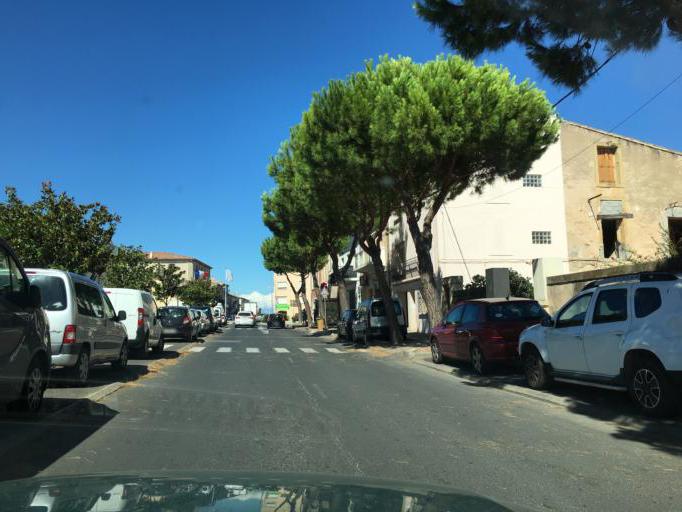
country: FR
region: Languedoc-Roussillon
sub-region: Departement de l'Herault
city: Meze
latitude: 43.4268
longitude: 3.6042
